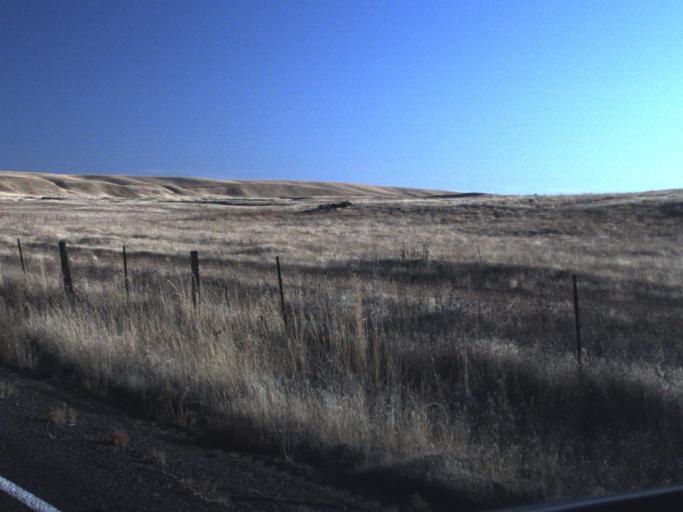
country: US
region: Washington
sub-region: Walla Walla County
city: Waitsburg
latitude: 46.6621
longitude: -118.2726
